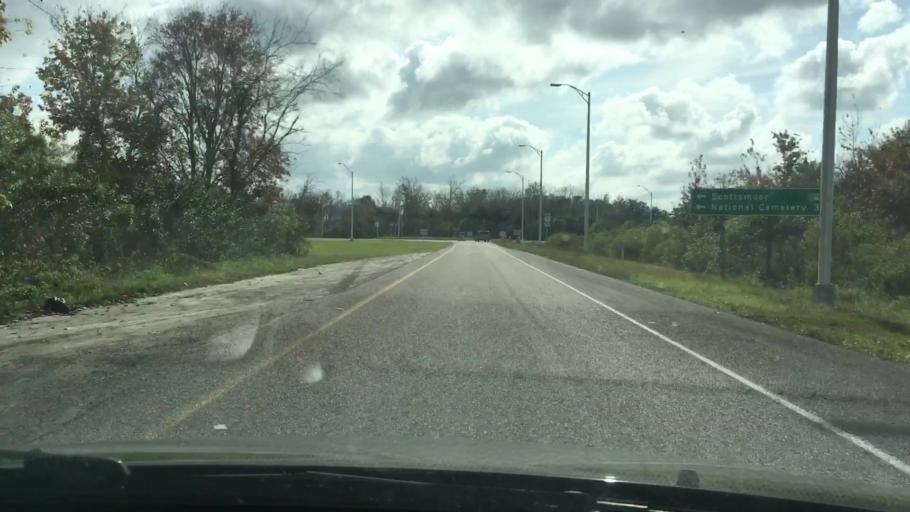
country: US
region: Florida
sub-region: Volusia County
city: Oak Hill
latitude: 28.7720
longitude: -80.8949
